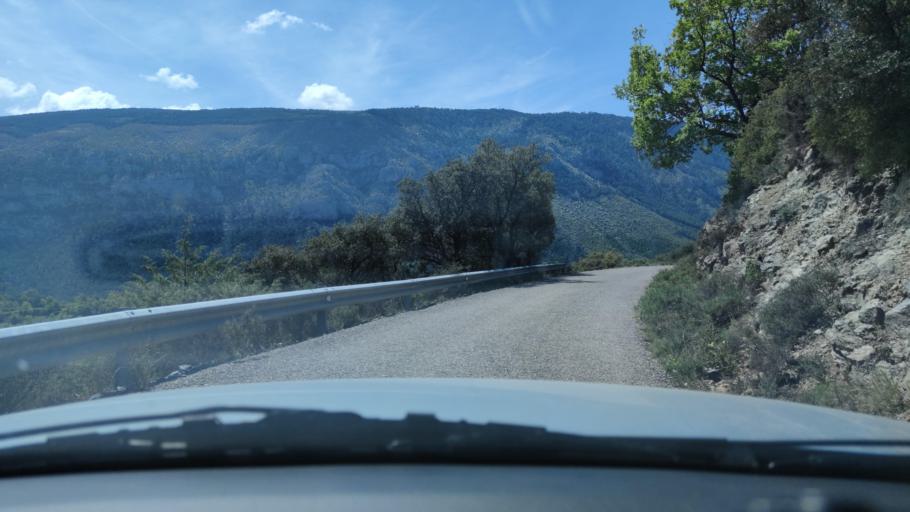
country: ES
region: Catalonia
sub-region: Provincia de Lleida
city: Sort
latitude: 42.3153
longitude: 1.0860
